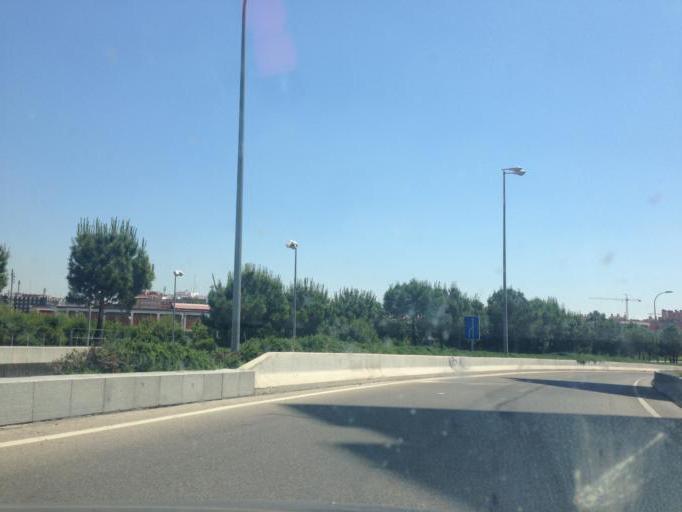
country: ES
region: Madrid
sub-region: Provincia de Madrid
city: Usera
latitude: 40.3881
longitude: -3.6988
